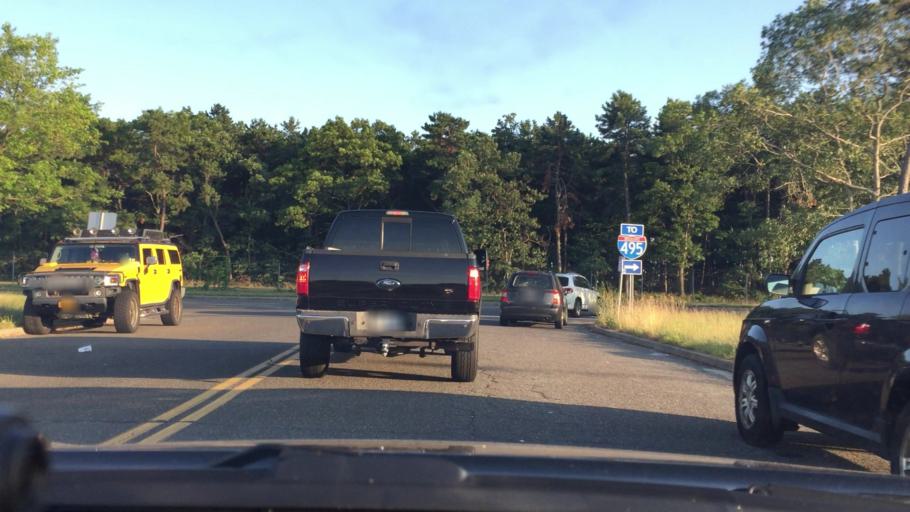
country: US
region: New York
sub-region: Suffolk County
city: Ronkonkoma
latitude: 40.8063
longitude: -73.1075
